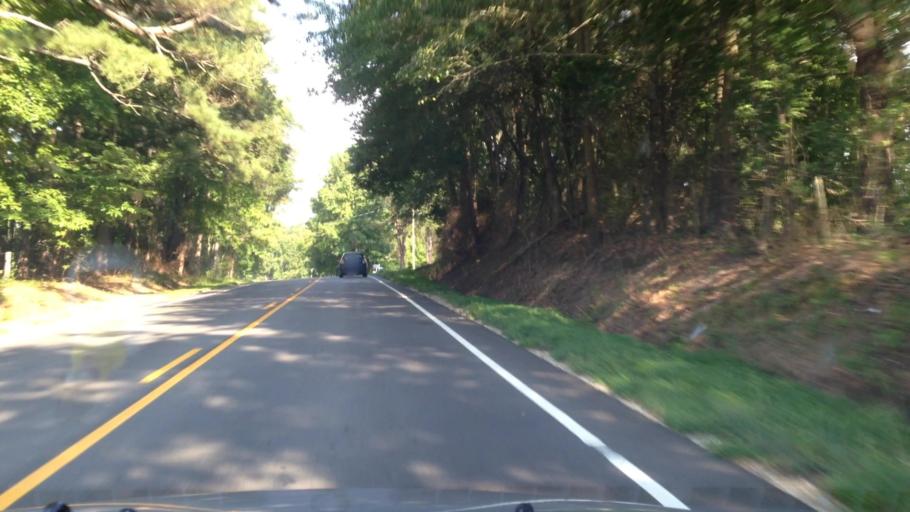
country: US
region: North Carolina
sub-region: Harnett County
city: Coats
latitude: 35.4123
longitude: -78.6901
